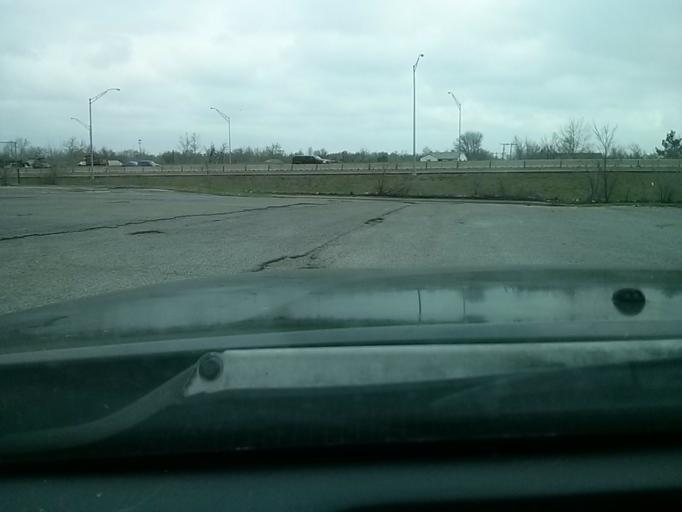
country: US
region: Oklahoma
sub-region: Tulsa County
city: Tulsa
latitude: 36.1618
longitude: -95.8985
